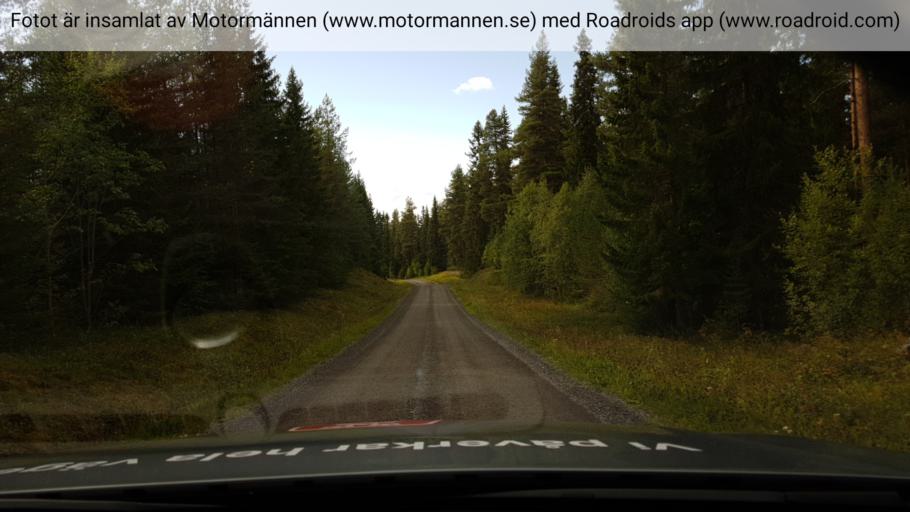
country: SE
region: Jaemtland
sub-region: OEstersunds Kommun
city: Lit
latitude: 63.3039
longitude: 15.2924
